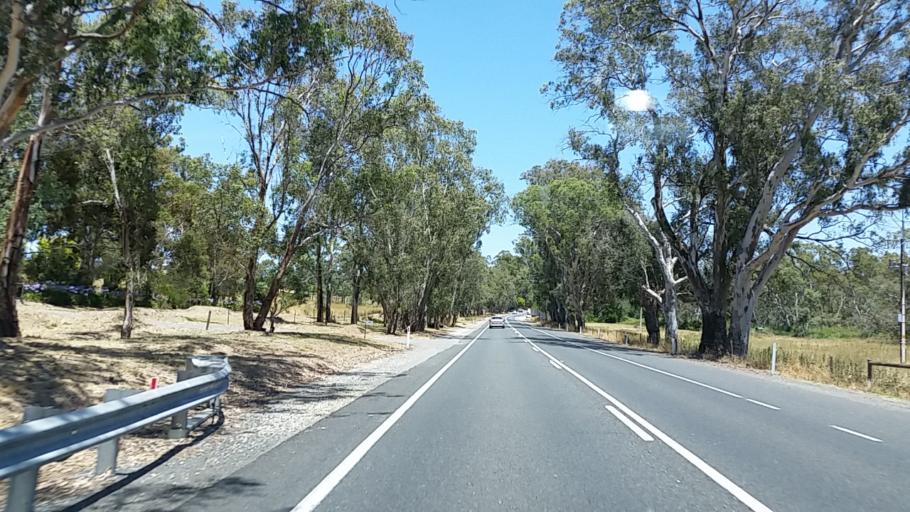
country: AU
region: South Australia
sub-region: Adelaide Hills
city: Birdwood
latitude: -34.8121
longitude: 138.9765
